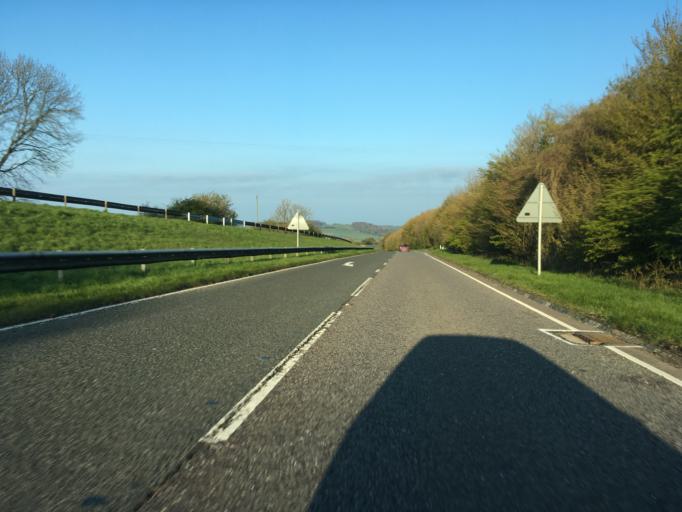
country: GB
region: England
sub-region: Gloucestershire
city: Shipton Village
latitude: 51.8589
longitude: -1.9342
